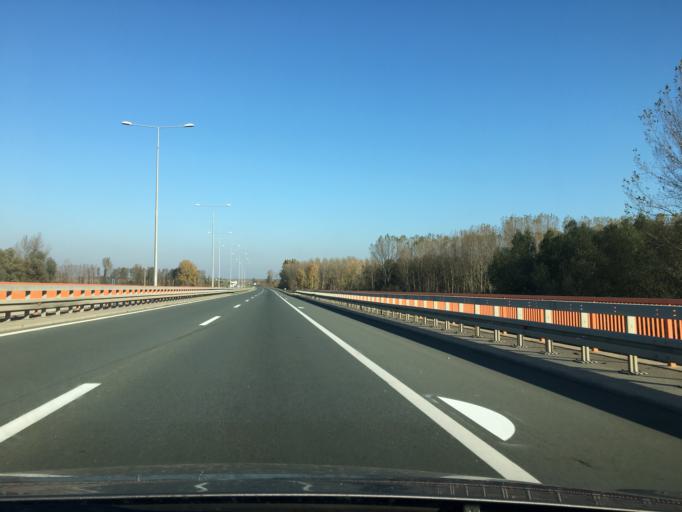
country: RS
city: Beska
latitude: 45.1841
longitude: 20.0775
